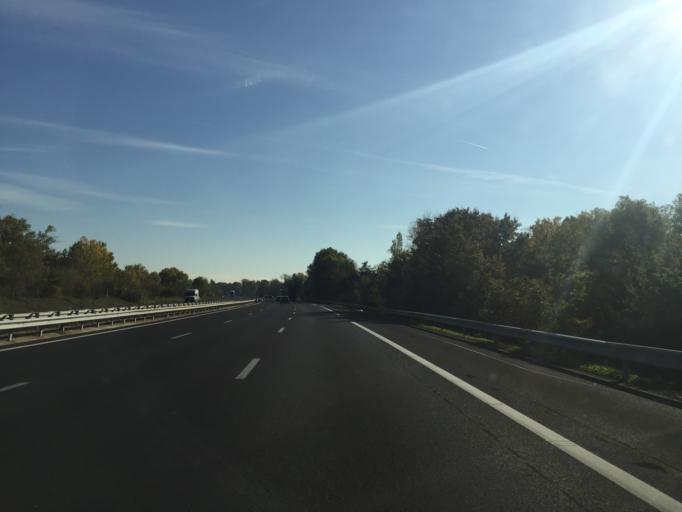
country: FR
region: Provence-Alpes-Cote d'Azur
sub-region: Departement des Bouches-du-Rhone
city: Cabannes
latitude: 43.8423
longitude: 4.9927
